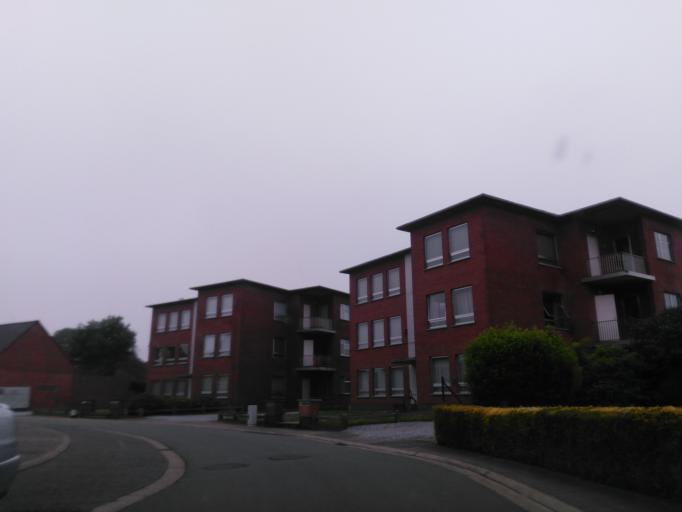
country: BE
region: Flanders
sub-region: Provincie Oost-Vlaanderen
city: Sint-Gillis-Waas
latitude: 51.2205
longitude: 4.1879
